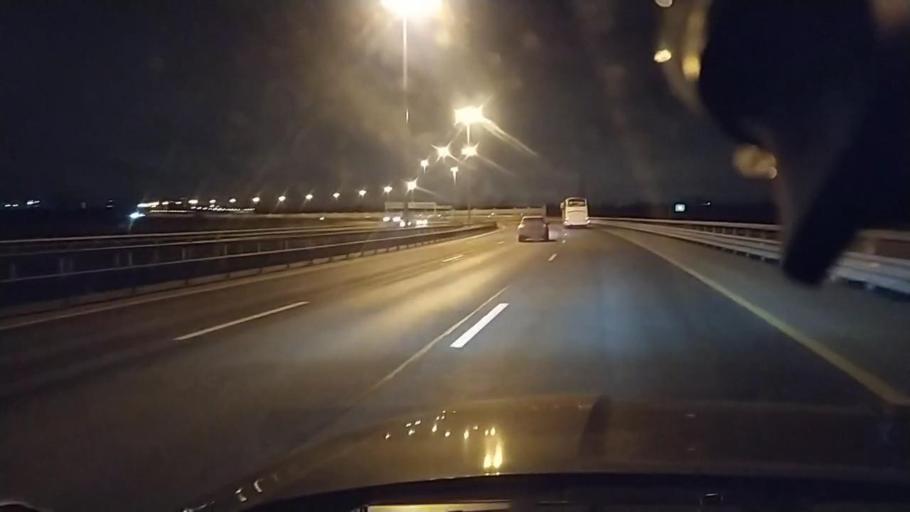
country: RU
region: St.-Petersburg
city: Lakhtinskiy
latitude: 60.0425
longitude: 30.1538
